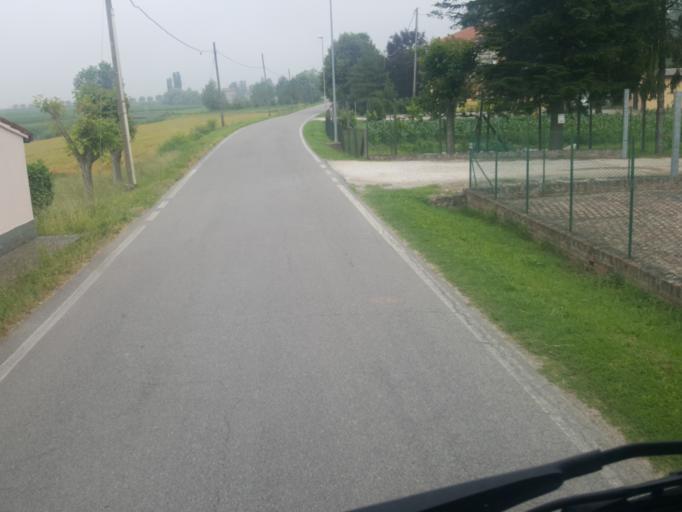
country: IT
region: Veneto
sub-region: Provincia di Rovigo
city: Canaro
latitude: 44.9341
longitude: 11.6566
